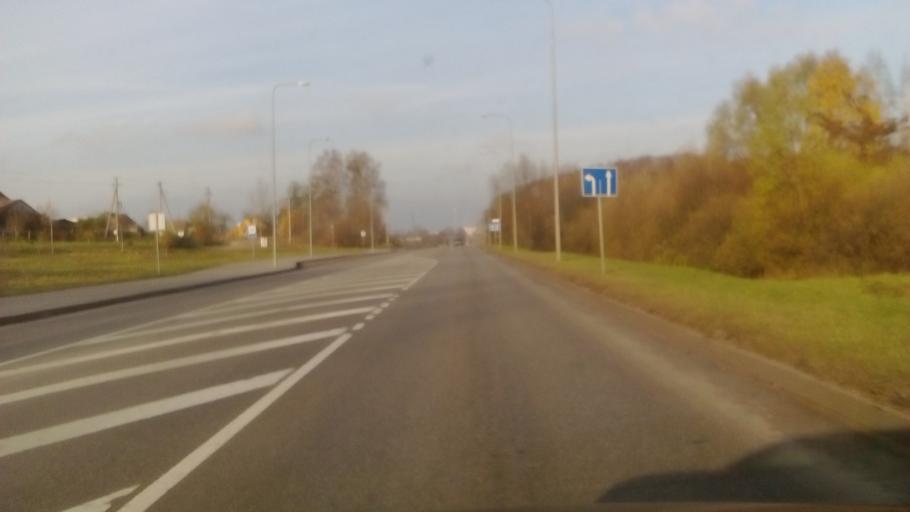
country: LT
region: Alytaus apskritis
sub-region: Alytus
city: Alytus
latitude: 54.3996
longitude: 24.0007
